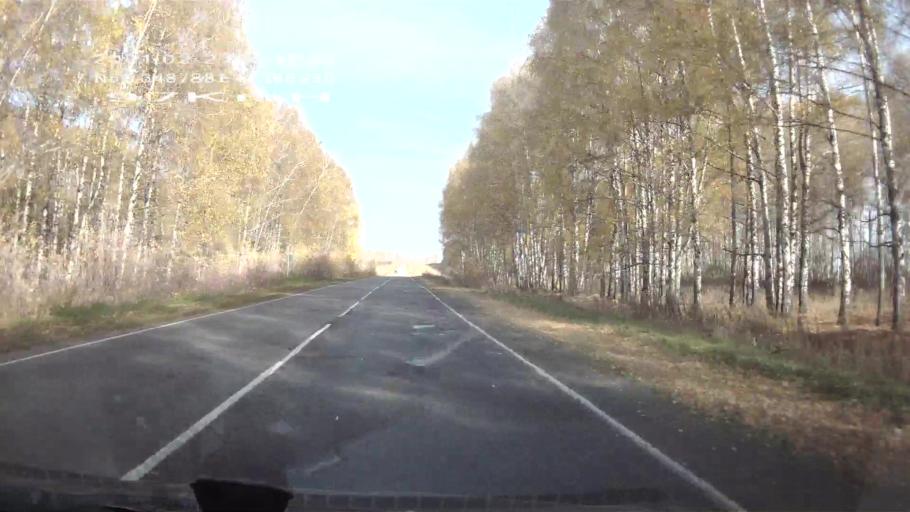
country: RU
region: Chuvashia
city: Ibresi
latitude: 55.3488
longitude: 47.1862
